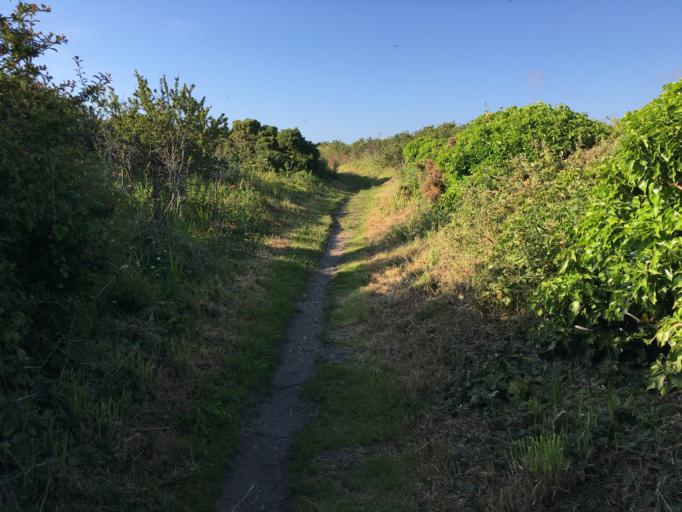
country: GB
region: England
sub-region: Cornwall
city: Saint Just
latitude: 50.1206
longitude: -5.6957
